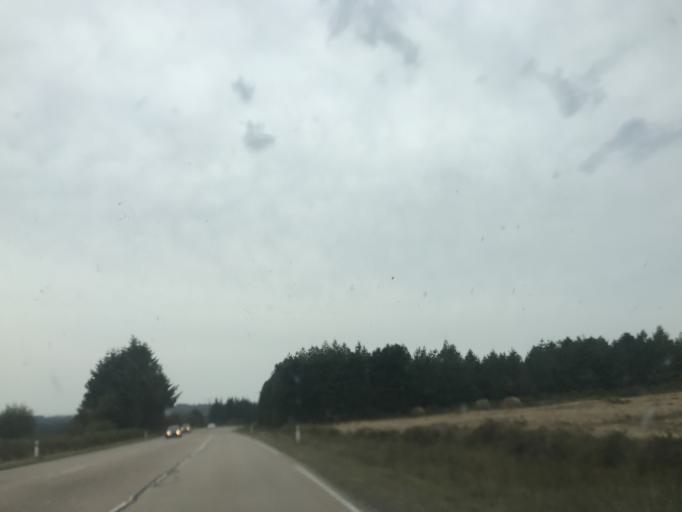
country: FR
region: Brittany
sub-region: Departement du Finistere
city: Plouneour-Menez
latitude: 48.4185
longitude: -3.8885
